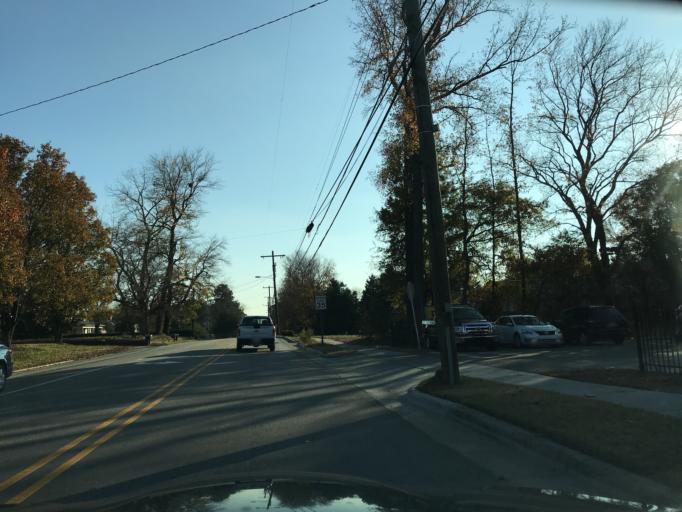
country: US
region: North Carolina
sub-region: Granville County
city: Creedmoor
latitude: 36.1165
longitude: -78.6870
